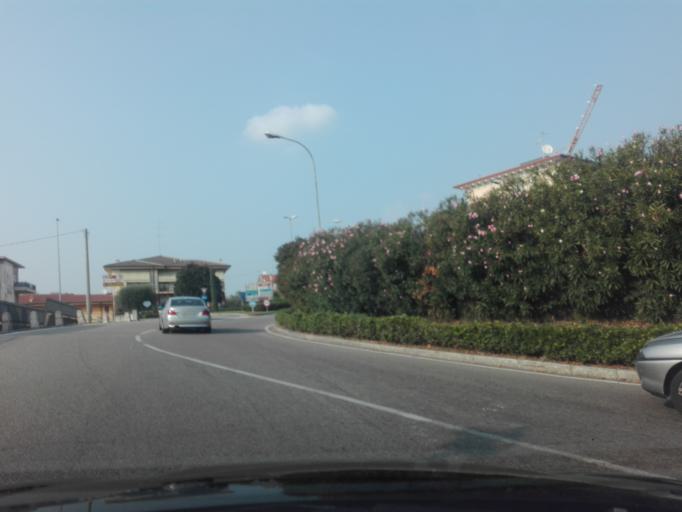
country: IT
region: Veneto
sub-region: Provincia di Verona
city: Peschiera del Garda
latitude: 45.4422
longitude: 10.7039
